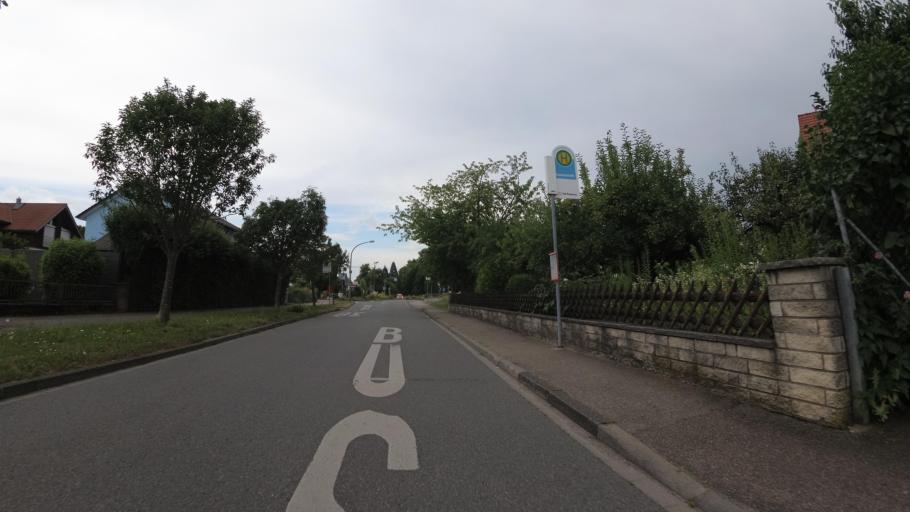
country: DE
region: Baden-Wuerttemberg
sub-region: Regierungsbezirk Stuttgart
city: Bad Rappenau
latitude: 49.2397
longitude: 9.0938
